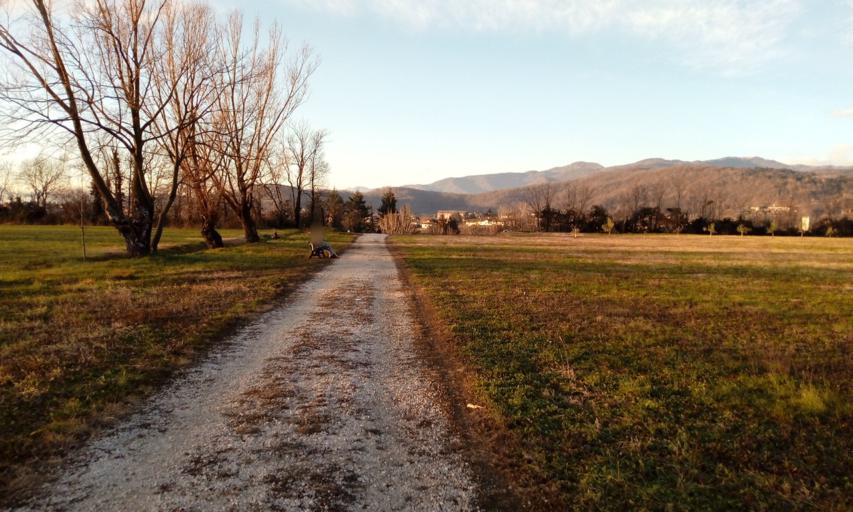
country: IT
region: Friuli Venezia Giulia
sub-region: Provincia di Udine
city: Cividale del Friuli
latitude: 46.0927
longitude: 13.4427
